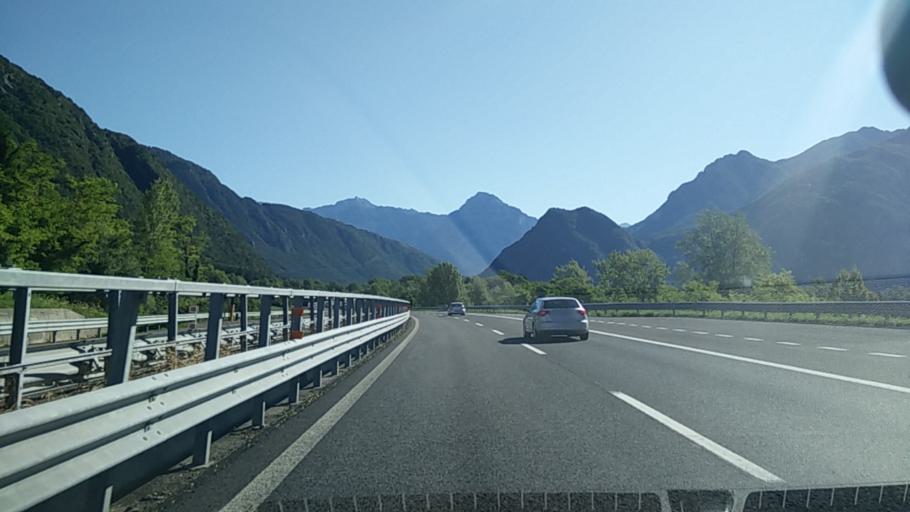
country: IT
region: Friuli Venezia Giulia
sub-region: Provincia di Udine
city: Amaro
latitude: 46.3723
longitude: 13.1016
